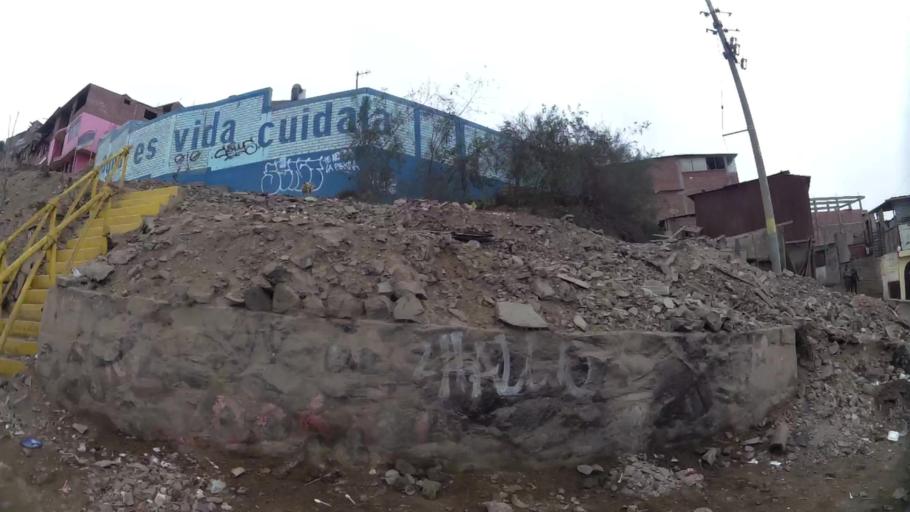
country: PE
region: Lima
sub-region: Lima
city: Surco
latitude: -12.1671
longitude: -76.9562
